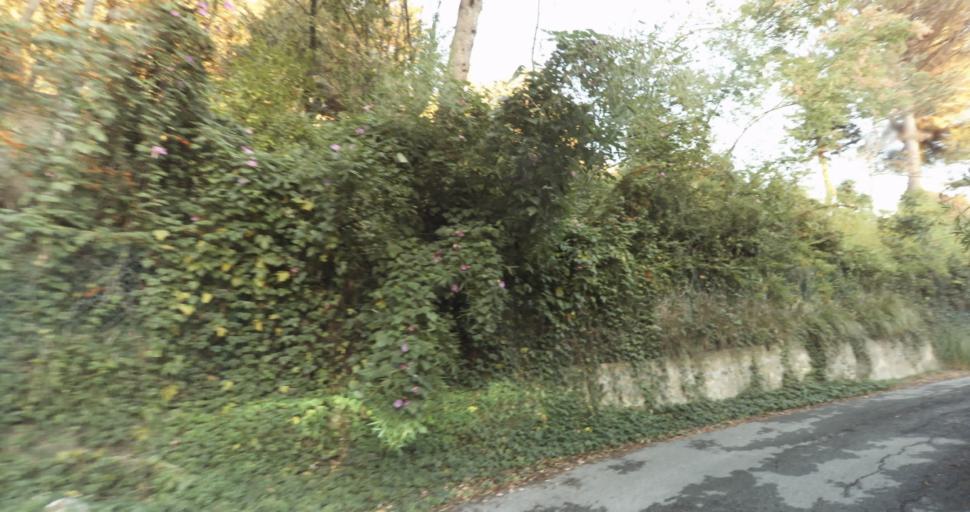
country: FR
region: Provence-Alpes-Cote d'Azur
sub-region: Departement des Alpes-Maritimes
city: Vence
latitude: 43.7296
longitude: 7.1047
